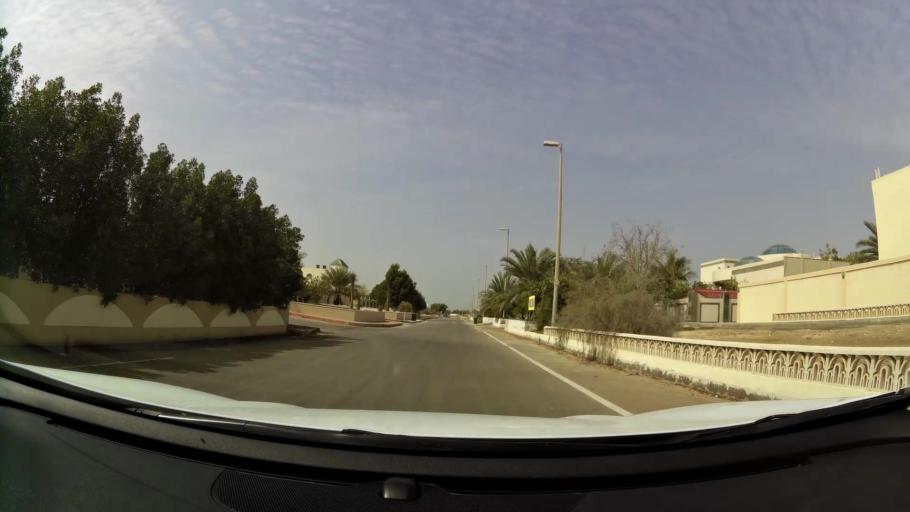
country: AE
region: Abu Dhabi
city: Abu Dhabi
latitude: 24.5179
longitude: 54.6637
